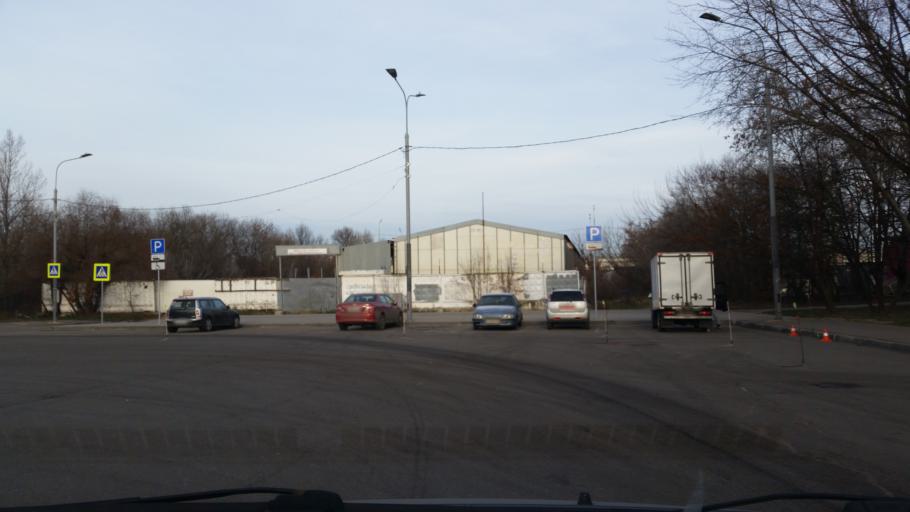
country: RU
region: Moskovskaya
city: Biryulevo Zapadnoye
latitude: 55.6029
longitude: 37.6312
